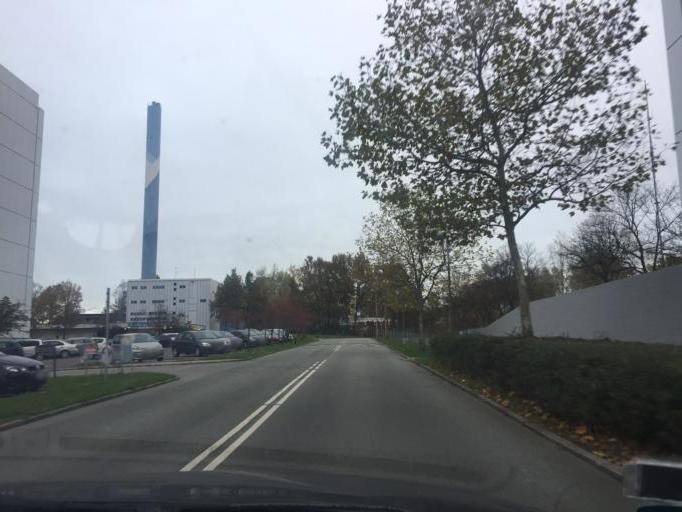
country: DK
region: Capital Region
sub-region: Gladsaxe Municipality
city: Buddinge
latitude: 55.7310
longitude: 12.4865
